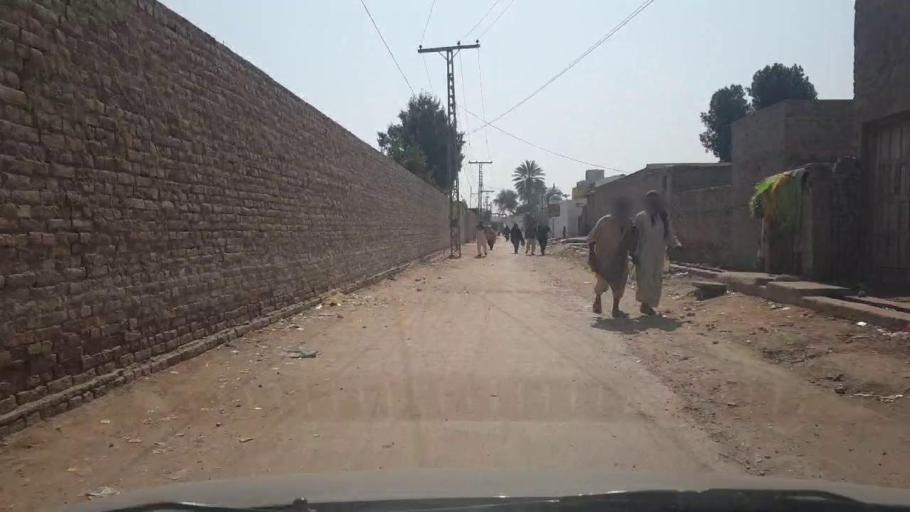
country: PK
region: Sindh
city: Mirwah Gorchani
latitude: 25.3129
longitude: 69.1548
